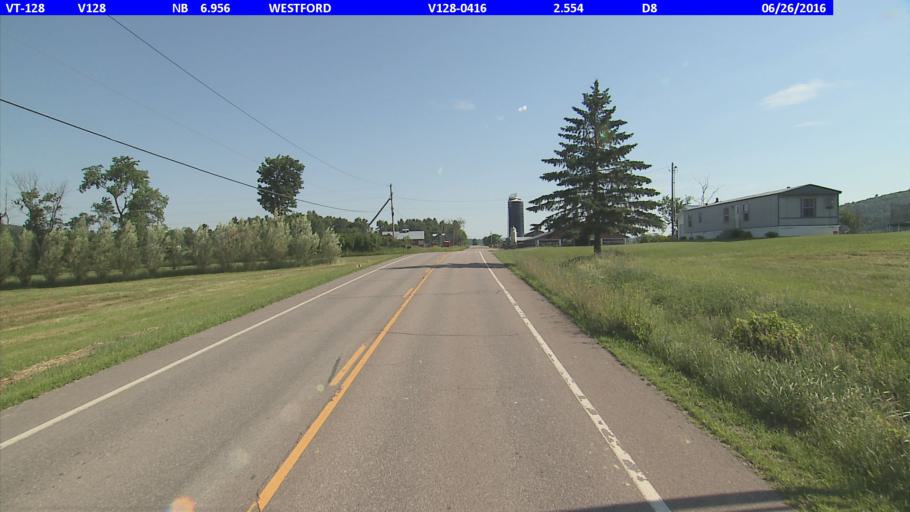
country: US
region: Vermont
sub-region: Chittenden County
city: Jericho
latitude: 44.5941
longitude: -73.0122
